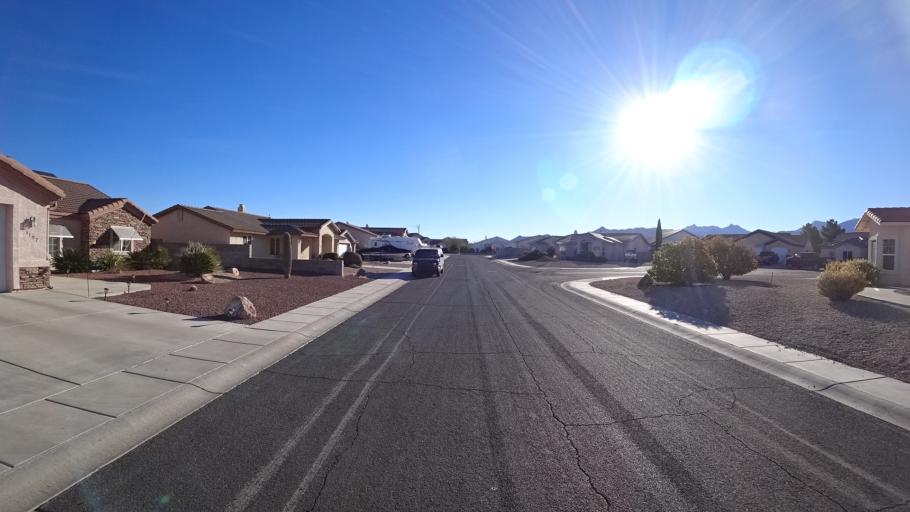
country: US
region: Arizona
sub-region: Mohave County
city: Kingman
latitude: 35.1952
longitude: -114.0045
